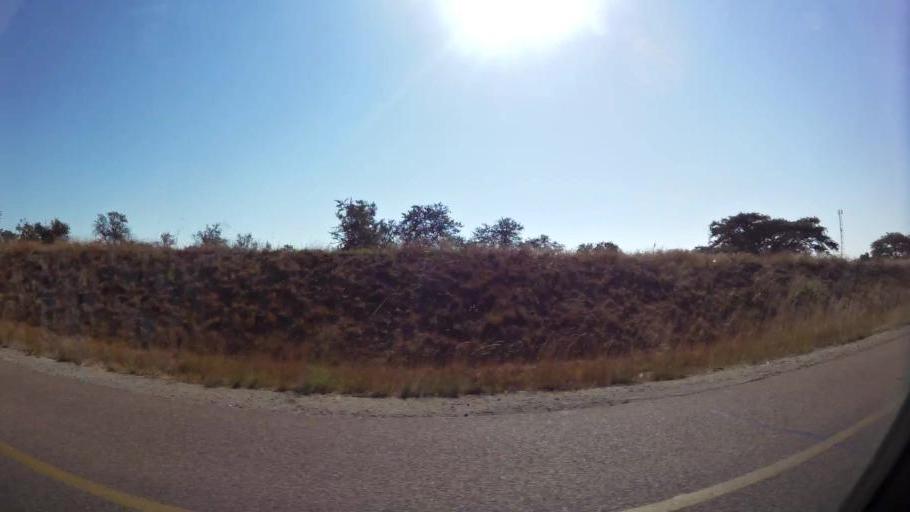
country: ZA
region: North-West
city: Ga-Rankuwa
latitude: -25.6573
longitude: 28.0780
